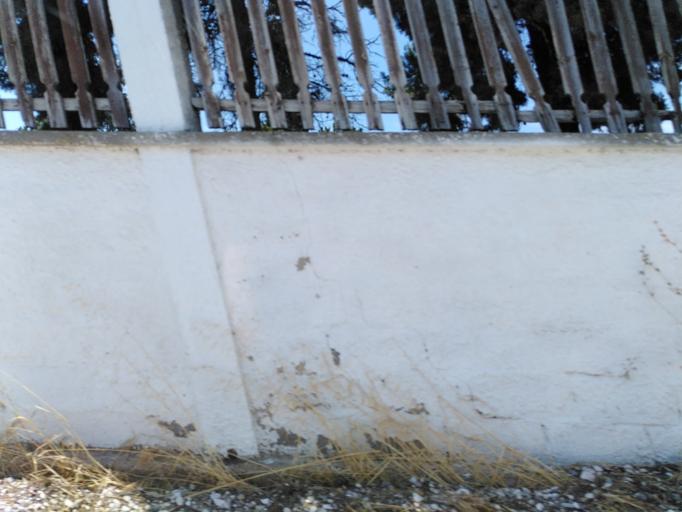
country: GR
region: Central Macedonia
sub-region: Nomos Thessalonikis
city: Agia Triada
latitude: 40.5030
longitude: 22.8461
